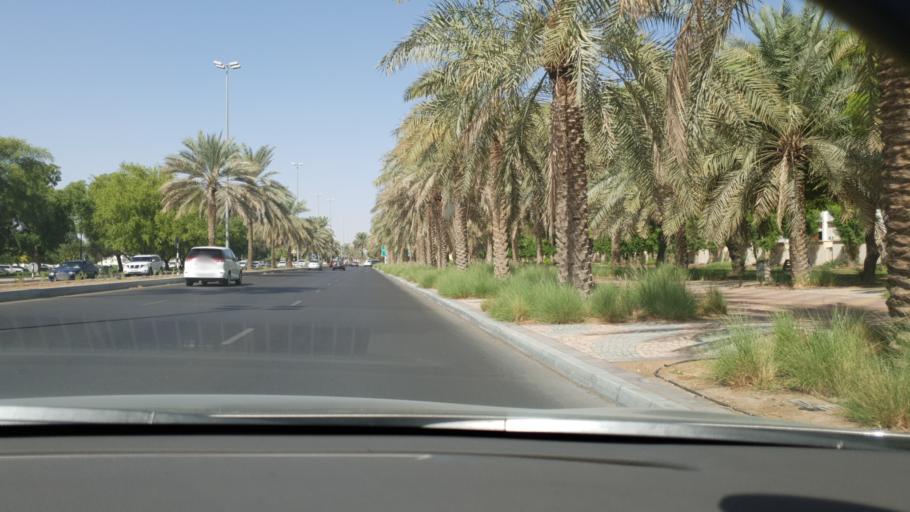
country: AE
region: Abu Dhabi
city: Al Ain
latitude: 24.2387
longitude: 55.7390
